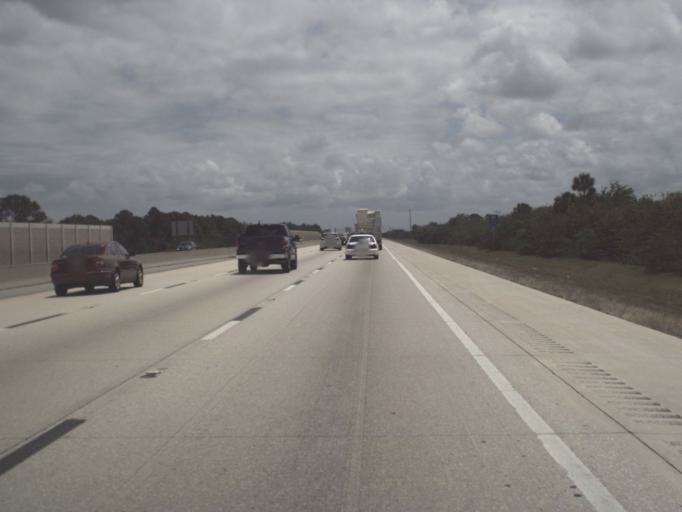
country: US
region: Florida
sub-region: Brevard County
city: Cocoa West
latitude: 28.3517
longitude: -80.7895
